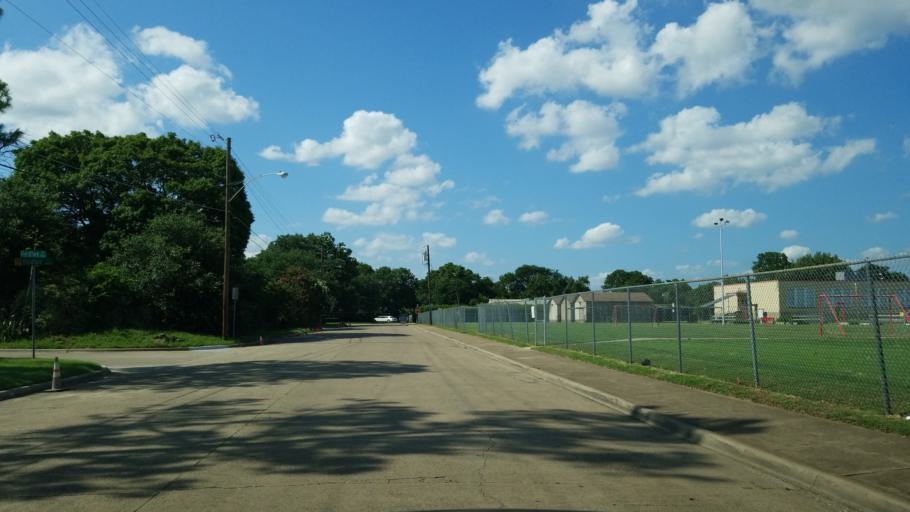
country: US
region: Texas
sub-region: Dallas County
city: University Park
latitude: 32.8822
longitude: -96.8407
